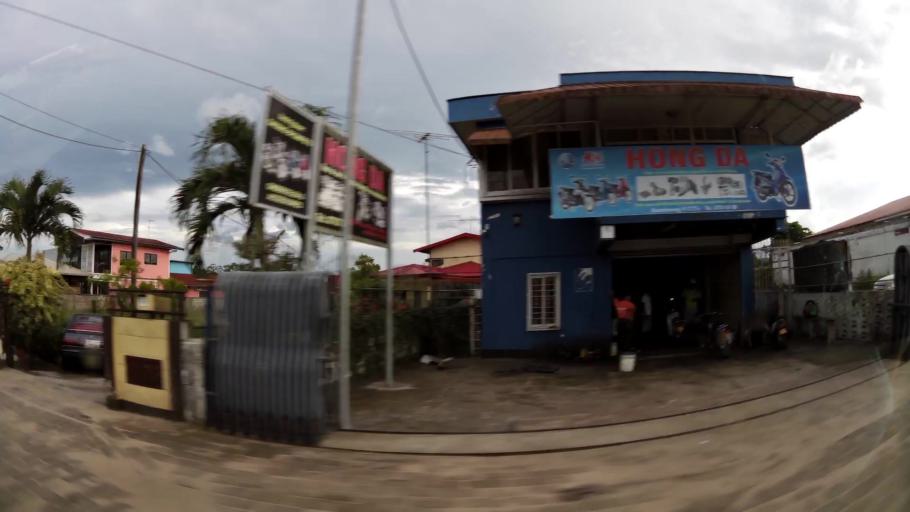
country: SR
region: Paramaribo
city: Paramaribo
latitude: 5.8390
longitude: -55.1806
